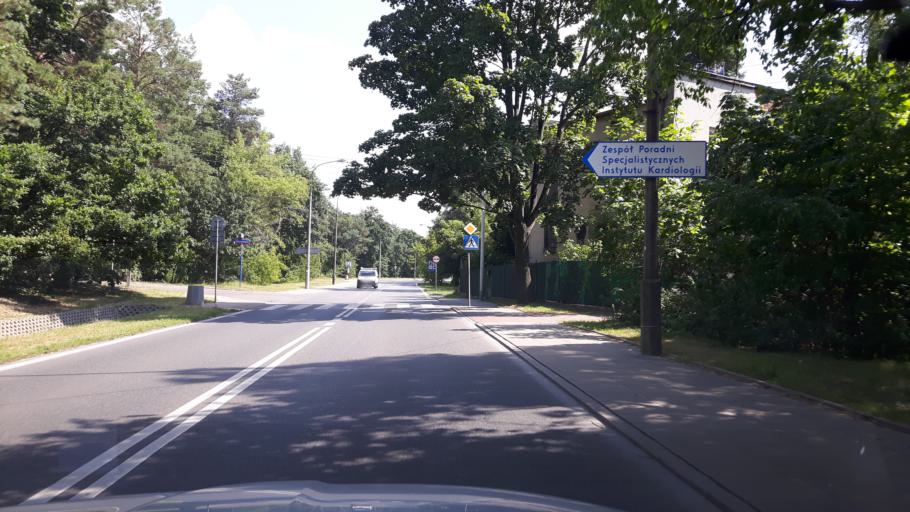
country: PL
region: Masovian Voivodeship
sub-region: Warszawa
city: Wawer
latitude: 52.2106
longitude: 21.1682
